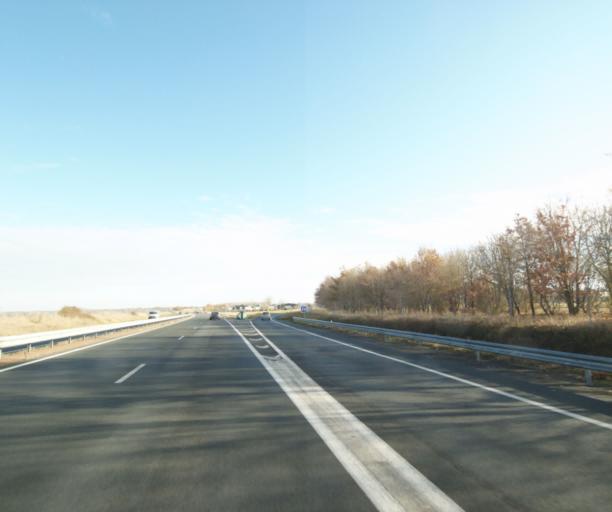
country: FR
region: Poitou-Charentes
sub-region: Departement de la Charente-Maritime
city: Corme-Royal
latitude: 45.7008
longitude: -0.7958
